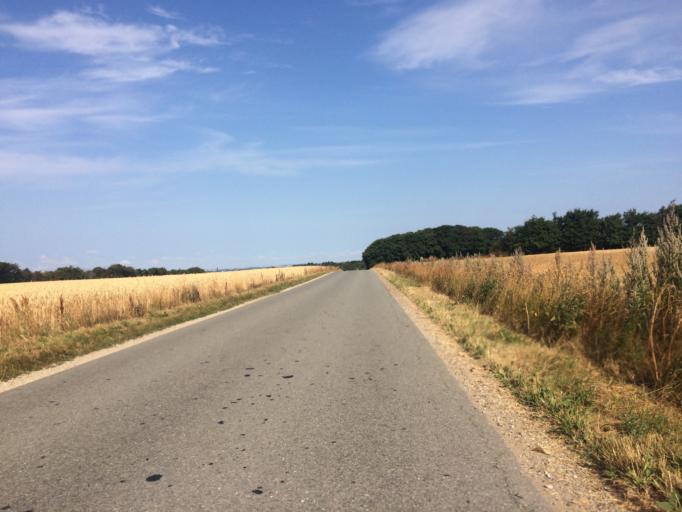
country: DK
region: North Denmark
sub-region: Morso Kommune
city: Nykobing Mors
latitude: 56.6496
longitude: 8.7924
